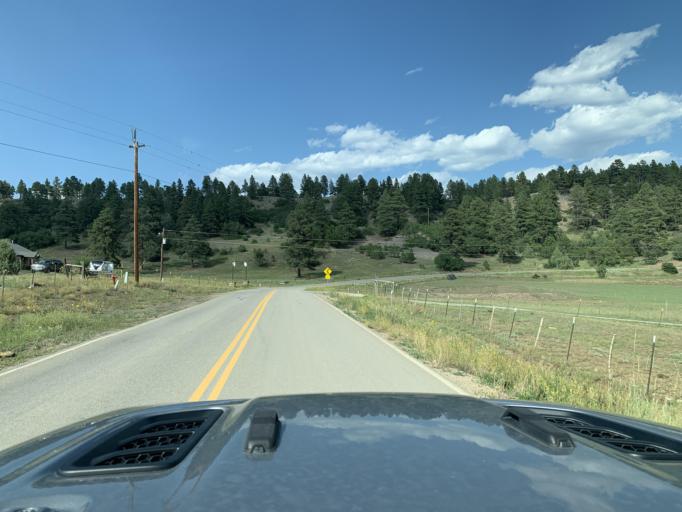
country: US
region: Colorado
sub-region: Archuleta County
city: Pagosa Springs
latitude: 37.2437
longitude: -107.0344
